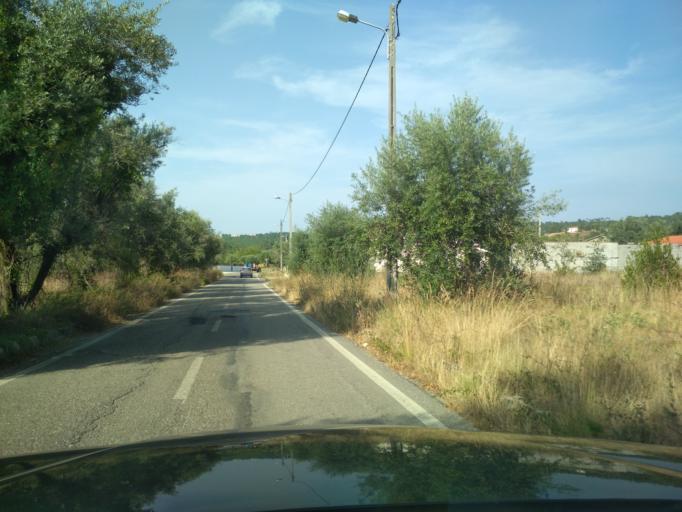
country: PT
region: Coimbra
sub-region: Condeixa-A-Nova
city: Condeixa-a-Nova
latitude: 40.1350
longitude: -8.4592
